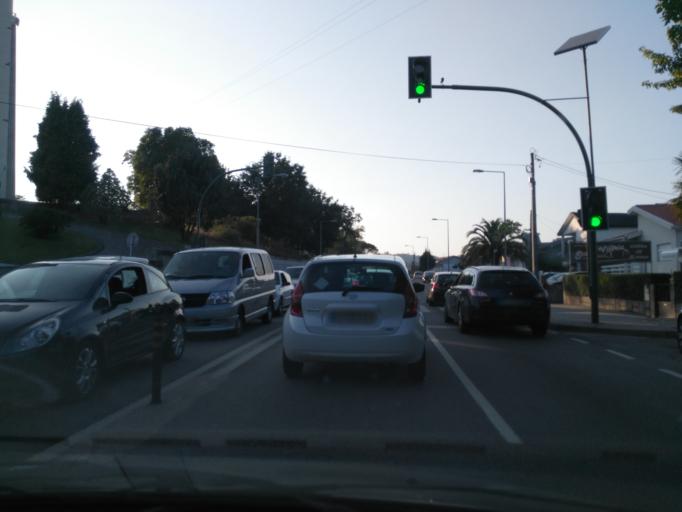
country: PT
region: Braga
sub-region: Guimaraes
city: Candoso
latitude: 41.4443
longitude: -8.3361
